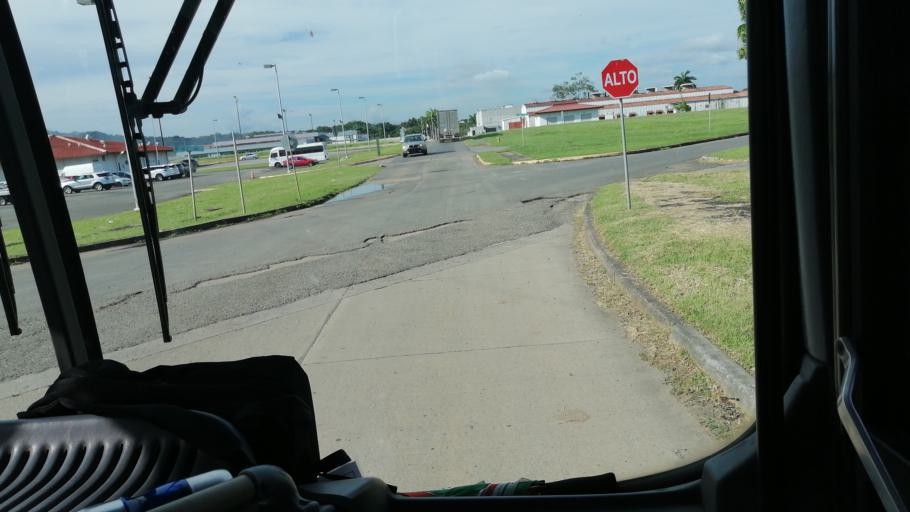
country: PA
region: Panama
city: Veracruz
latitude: 8.9171
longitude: -79.5944
